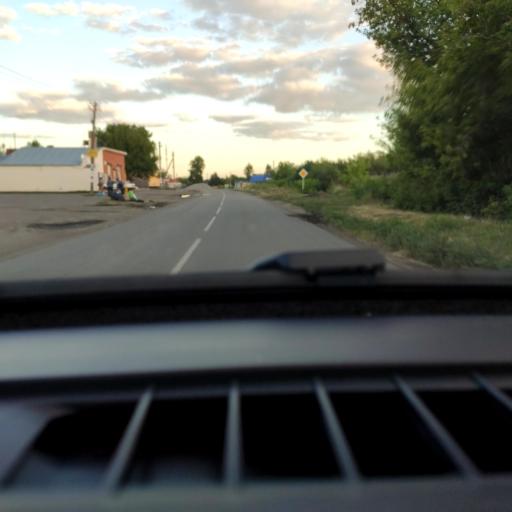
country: RU
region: Voronezj
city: Orlovo
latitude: 51.6620
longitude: 39.6934
